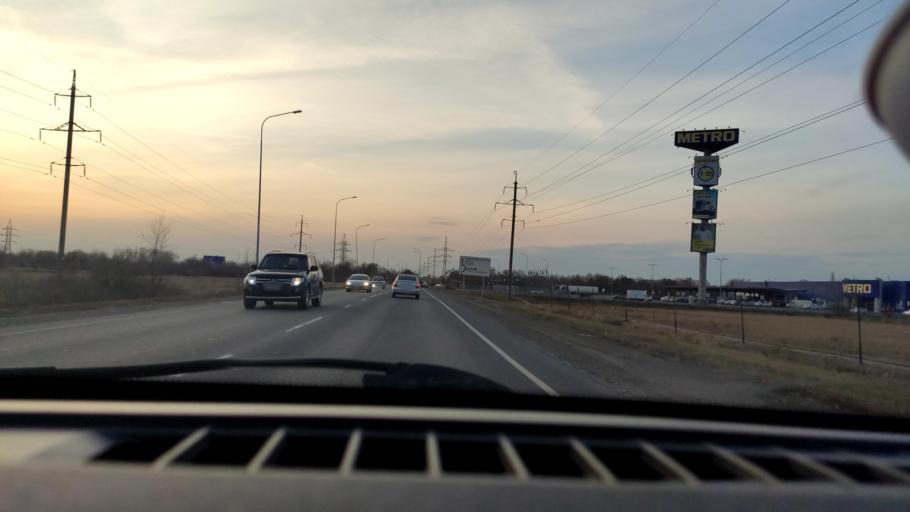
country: RU
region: Samara
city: Samara
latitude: 53.1315
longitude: 50.1418
